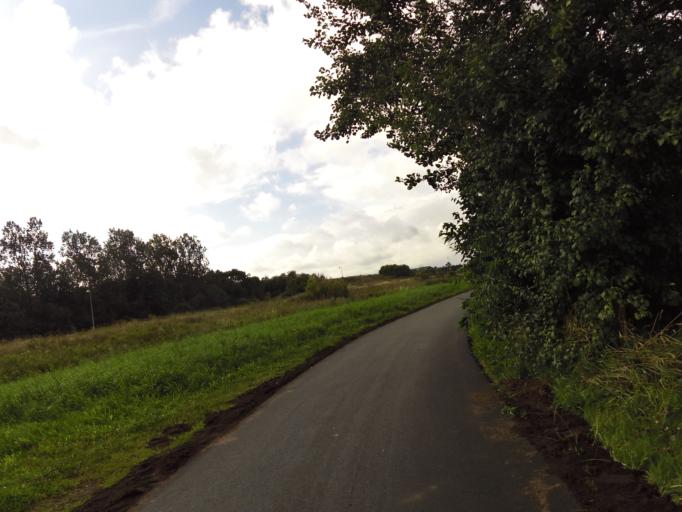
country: DK
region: South Denmark
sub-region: Esbjerg Kommune
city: Ribe
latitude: 55.3357
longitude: 8.7802
